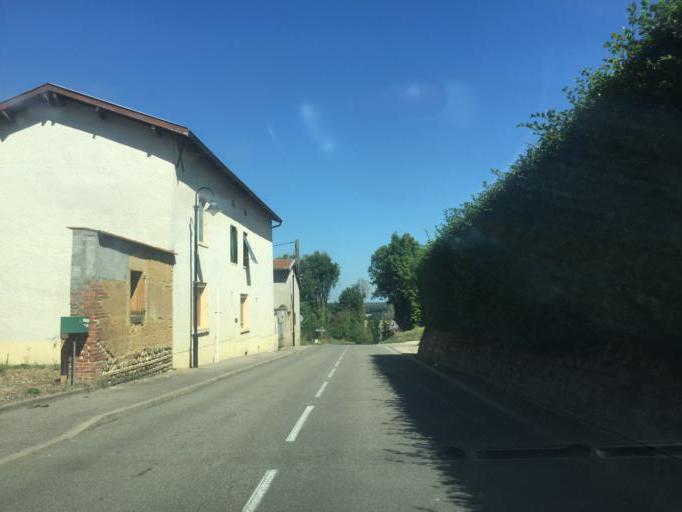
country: FR
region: Rhone-Alpes
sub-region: Departement de l'Ain
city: Tramoyes
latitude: 45.8782
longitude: 4.9687
